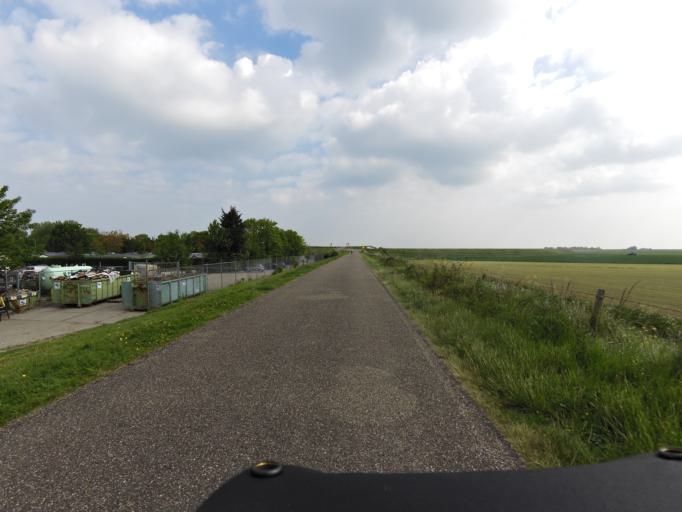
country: NL
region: Zeeland
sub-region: Gemeente Noord-Beveland
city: Kamperland
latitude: 51.5899
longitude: 3.7314
